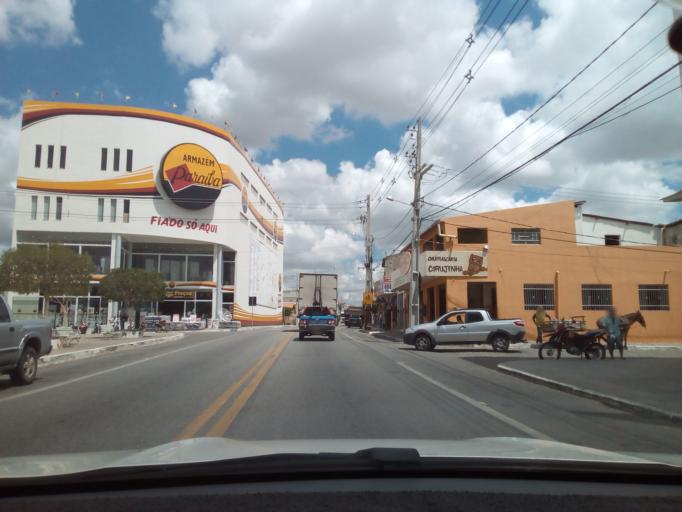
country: BR
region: Paraiba
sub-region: Soledade
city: Soledade
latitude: -7.0577
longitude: -36.3638
